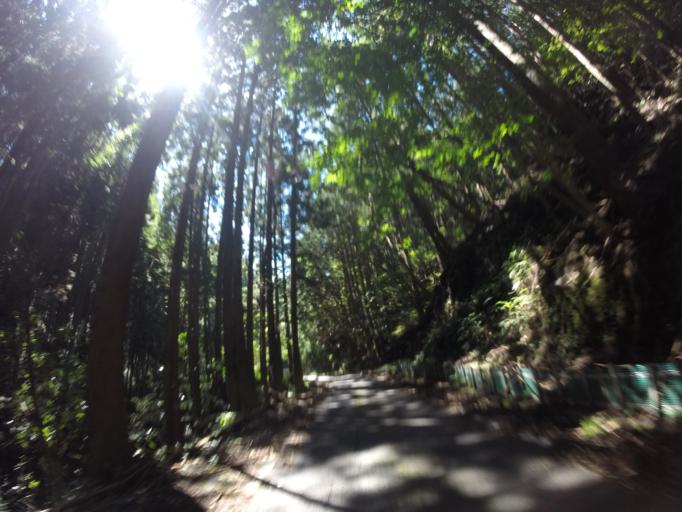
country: JP
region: Shizuoka
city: Shimada
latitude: 34.9064
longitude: 138.1688
